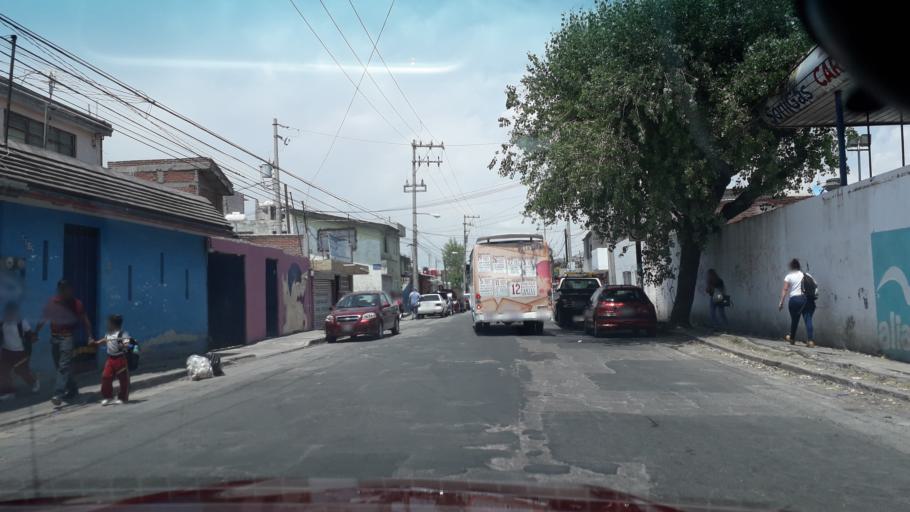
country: MX
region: Puebla
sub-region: Puebla
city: El Capulo (La Quebradora)
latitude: 18.9898
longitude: -98.2471
